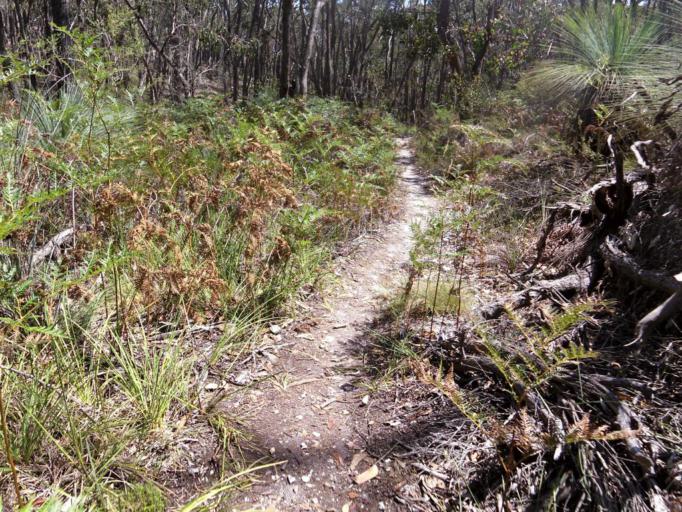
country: AU
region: Victoria
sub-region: Melton
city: Melton West
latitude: -37.5174
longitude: 144.5560
